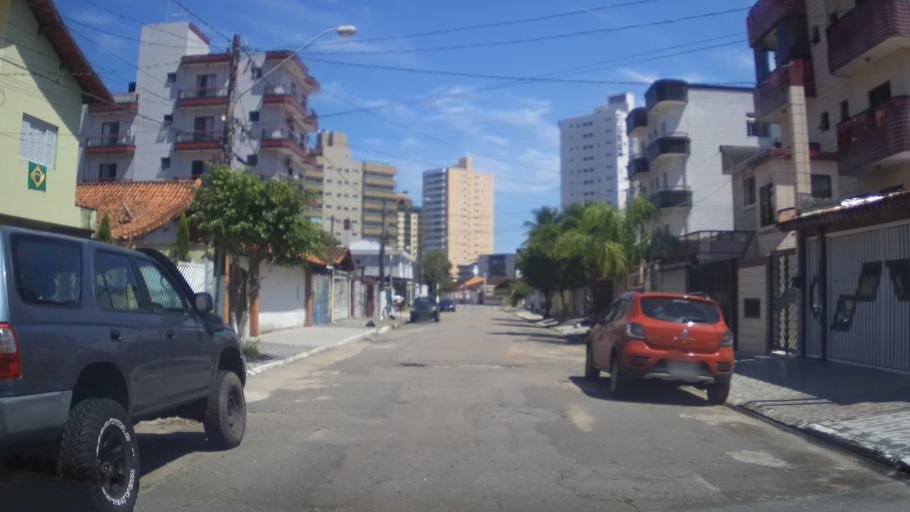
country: BR
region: Sao Paulo
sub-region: Praia Grande
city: Praia Grande
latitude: -24.0207
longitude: -46.4621
